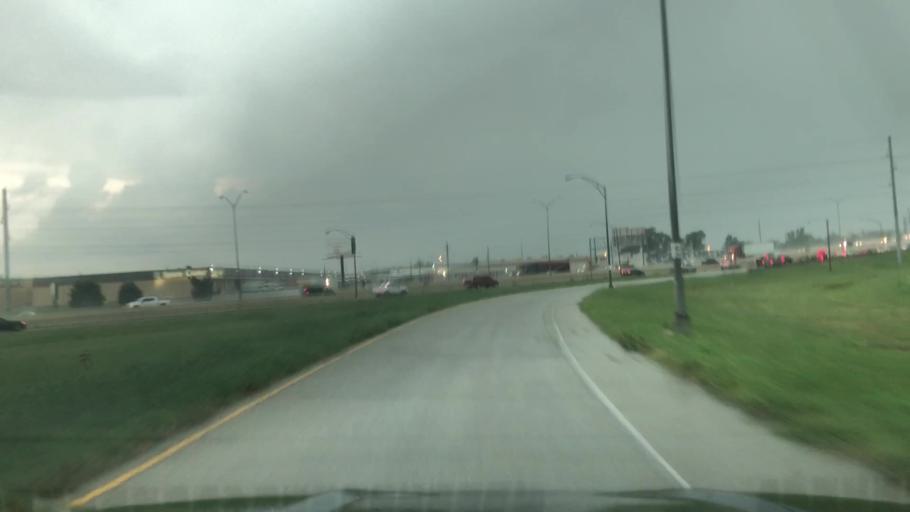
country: US
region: Oklahoma
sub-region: Tulsa County
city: Tulsa
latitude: 36.1132
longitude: -95.8987
